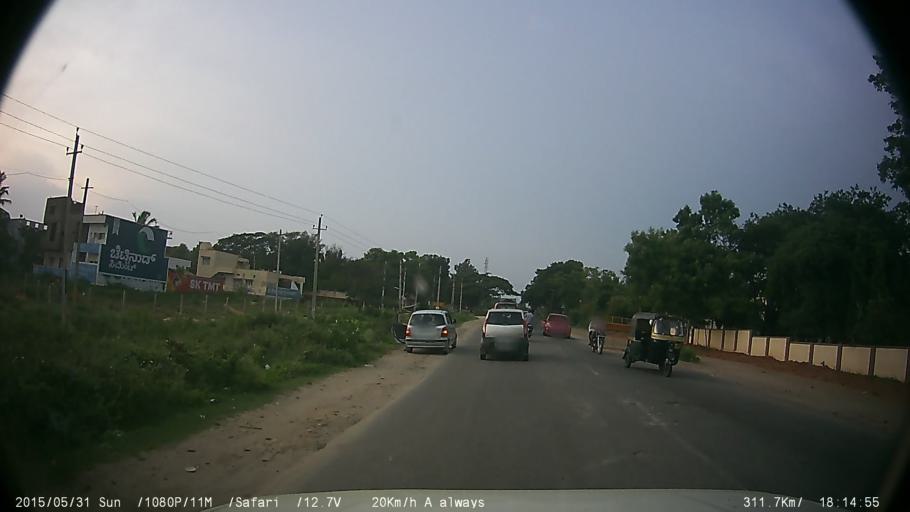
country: IN
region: Karnataka
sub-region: Mysore
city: Nanjangud
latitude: 12.1088
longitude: 76.6733
